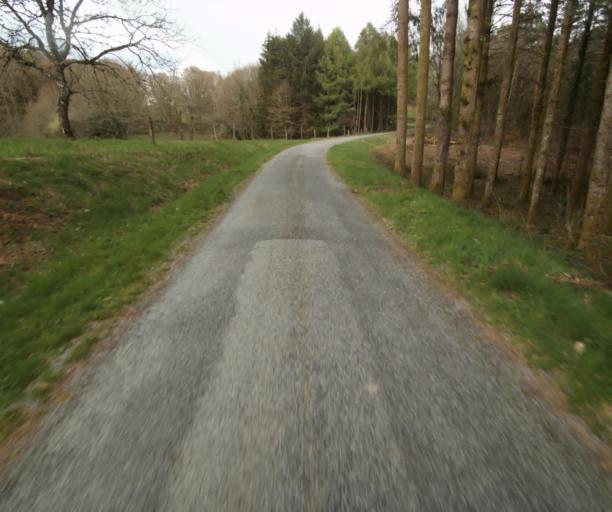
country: FR
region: Limousin
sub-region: Departement de la Correze
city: Argentat
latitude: 45.1995
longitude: 1.9848
